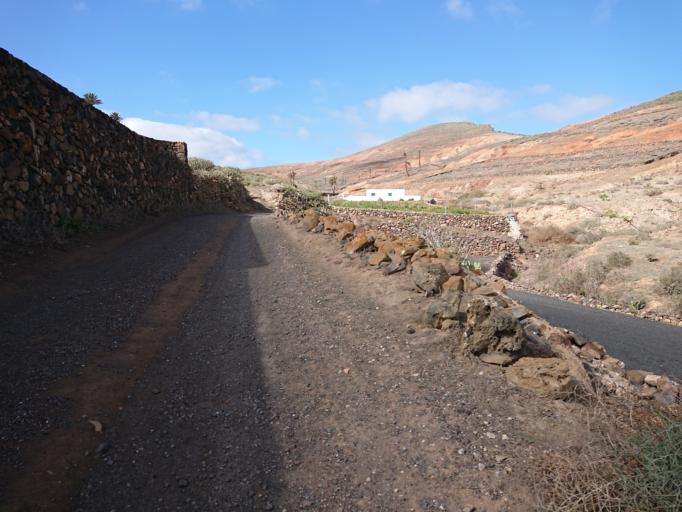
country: ES
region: Canary Islands
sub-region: Provincia de Las Palmas
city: Haria
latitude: 29.1444
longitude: -13.5101
